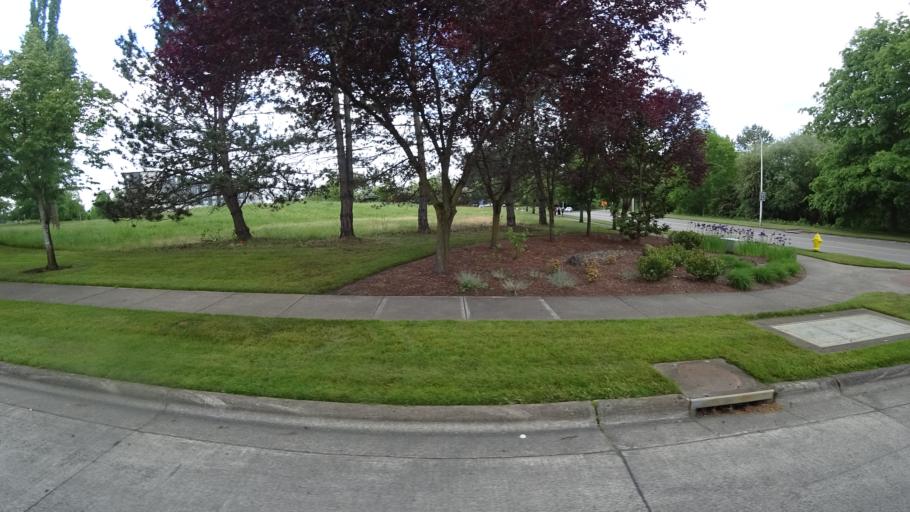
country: US
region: Oregon
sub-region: Washington County
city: Rockcreek
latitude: 45.5345
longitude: -122.8823
